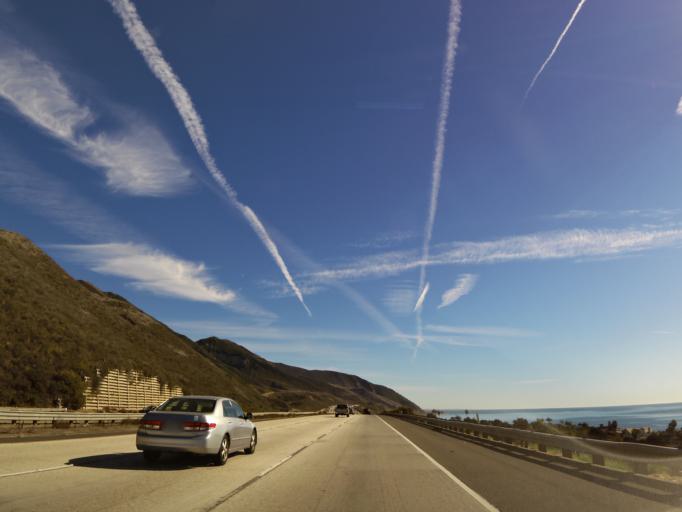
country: US
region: California
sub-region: Ventura County
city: Ventura
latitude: 34.3148
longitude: -119.3609
